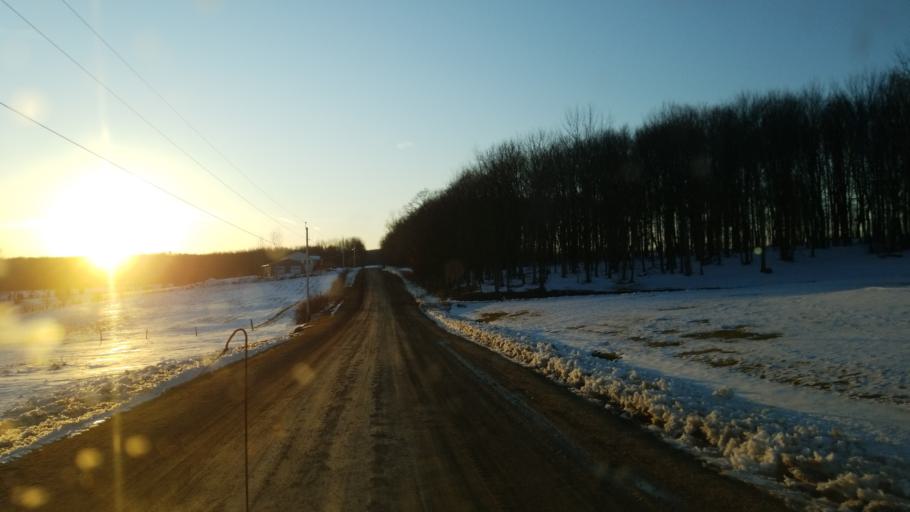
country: US
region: Pennsylvania
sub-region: Tioga County
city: Westfield
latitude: 42.0393
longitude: -77.6120
